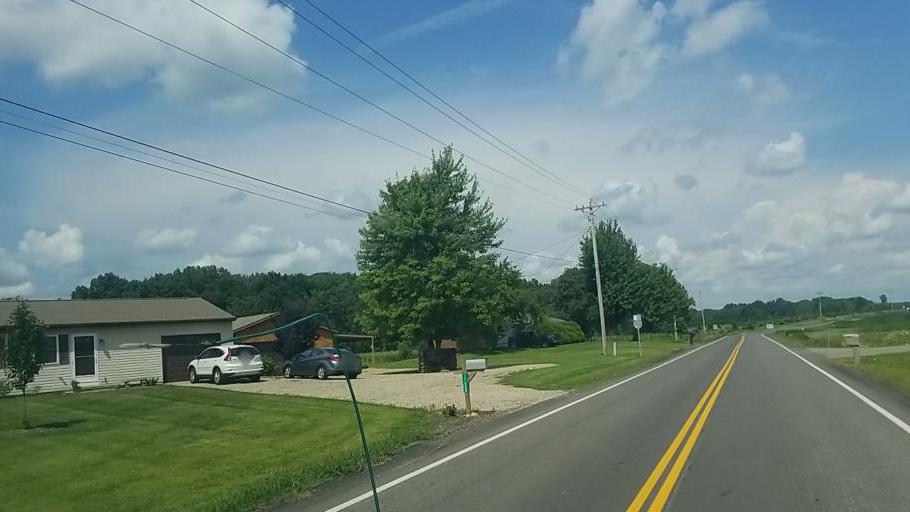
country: US
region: Ohio
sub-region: Wayne County
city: West Salem
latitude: 40.9505
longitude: -82.0835
